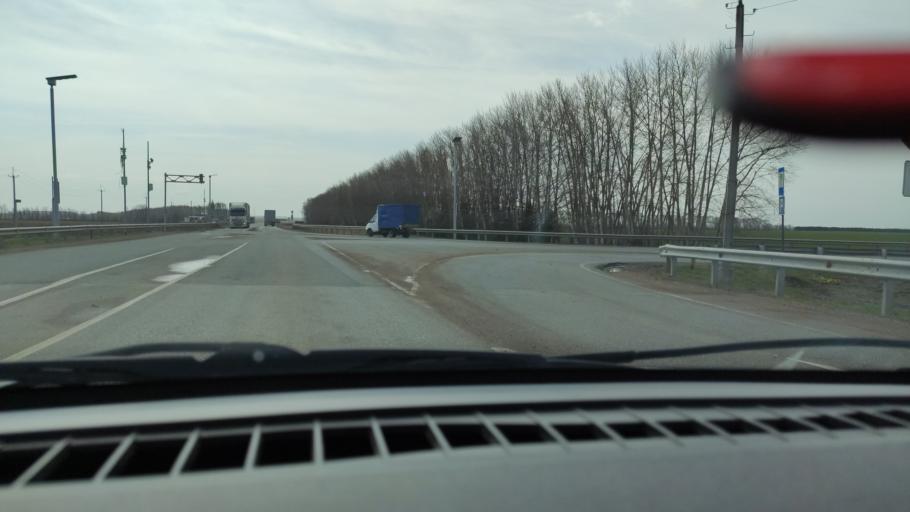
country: RU
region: Bashkortostan
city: Dyurtyuli
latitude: 55.4254
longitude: 54.8071
